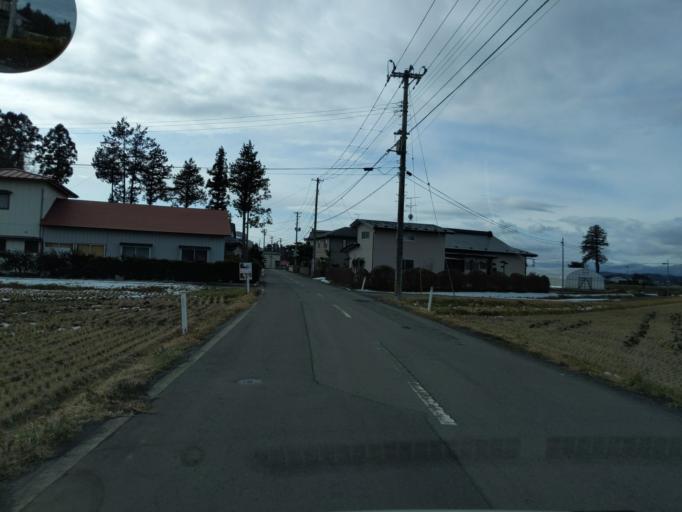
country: JP
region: Iwate
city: Mizusawa
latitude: 39.0892
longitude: 141.1746
